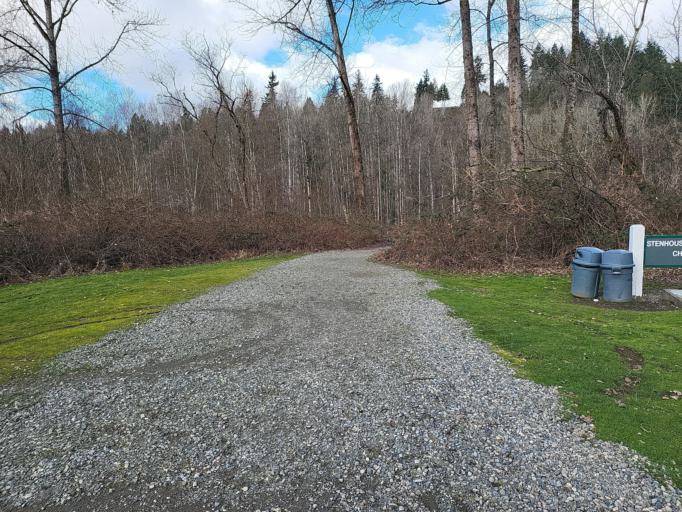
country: US
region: Washington
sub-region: King County
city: Fairwood
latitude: 47.4687
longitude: -122.1493
